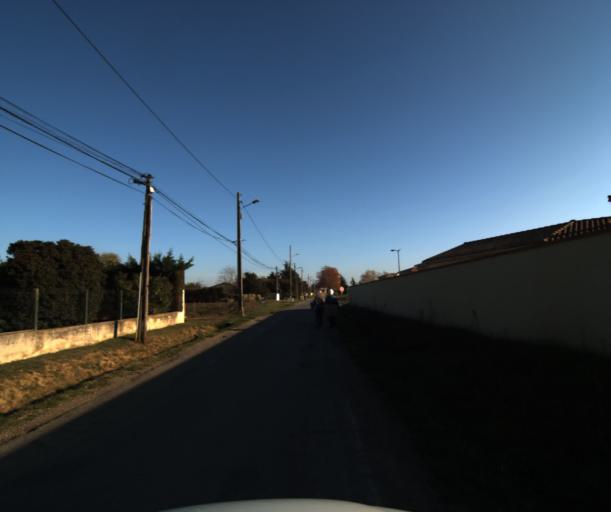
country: FR
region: Midi-Pyrenees
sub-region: Departement de la Haute-Garonne
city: Colomiers
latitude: 43.6257
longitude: 1.3231
